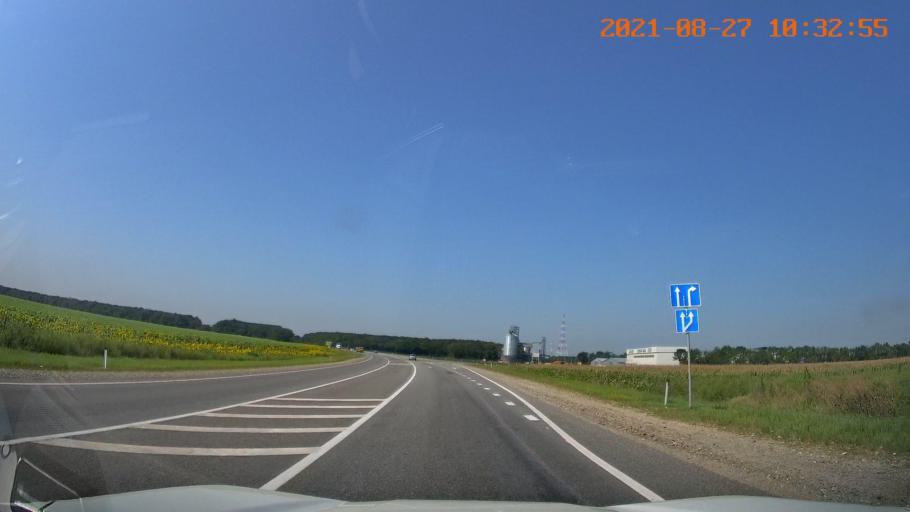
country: RU
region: Karachayevo-Cherkesiya
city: Cherkessk
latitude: 44.2627
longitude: 42.1290
